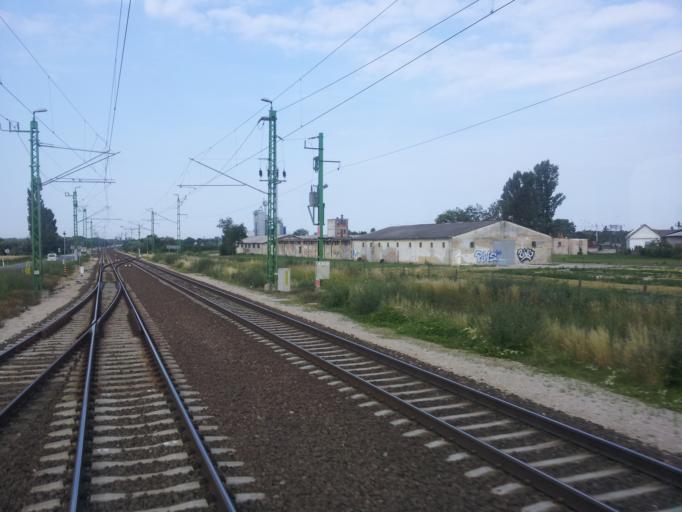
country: HU
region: Fejer
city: Kapolnasnyek
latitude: 47.2424
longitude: 18.6893
